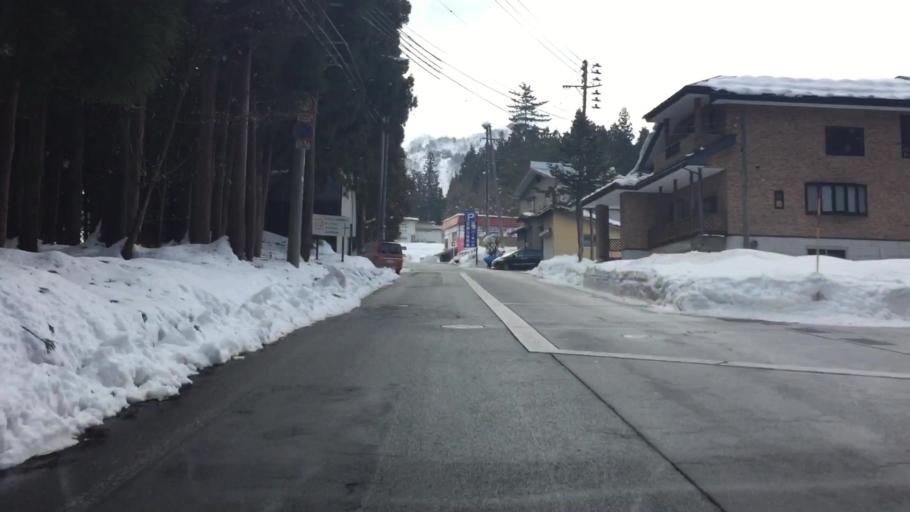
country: JP
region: Niigata
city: Shiozawa
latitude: 36.9882
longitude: 138.8218
